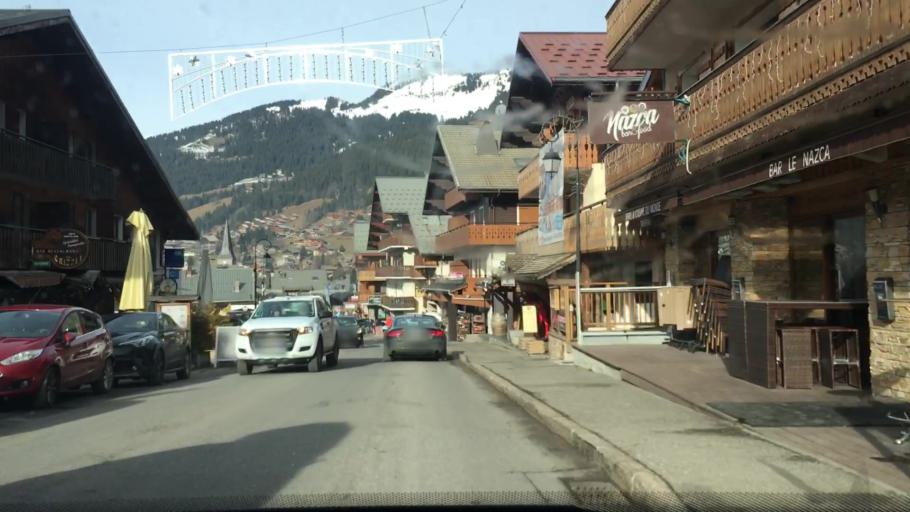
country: FR
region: Rhone-Alpes
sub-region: Departement de la Haute-Savoie
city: Chatel
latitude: 46.2652
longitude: 6.8417
